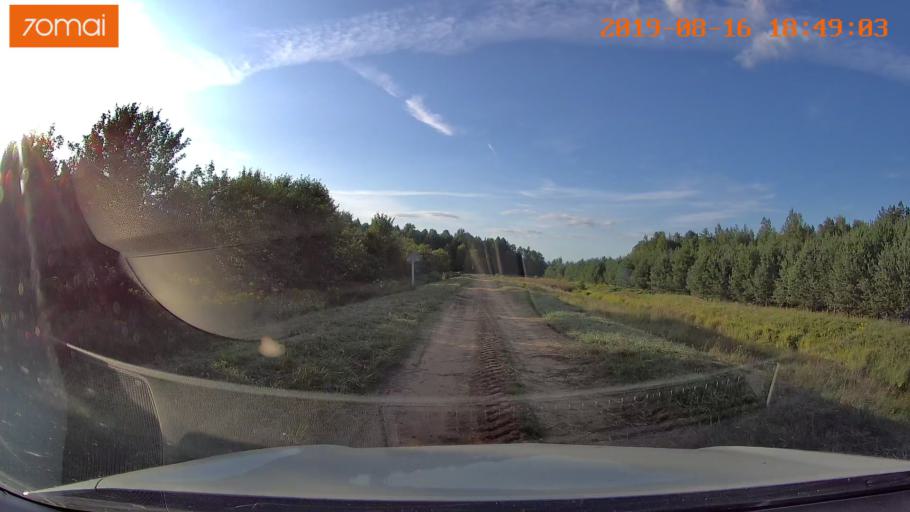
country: BY
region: Mogilev
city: Asipovichy
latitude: 53.2352
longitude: 28.6670
